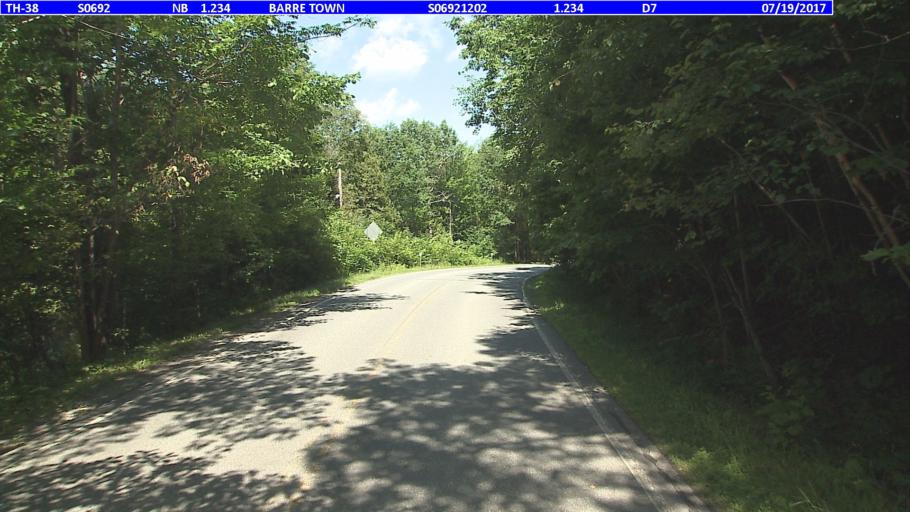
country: US
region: Vermont
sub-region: Washington County
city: South Barre
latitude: 44.1749
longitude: -72.4596
